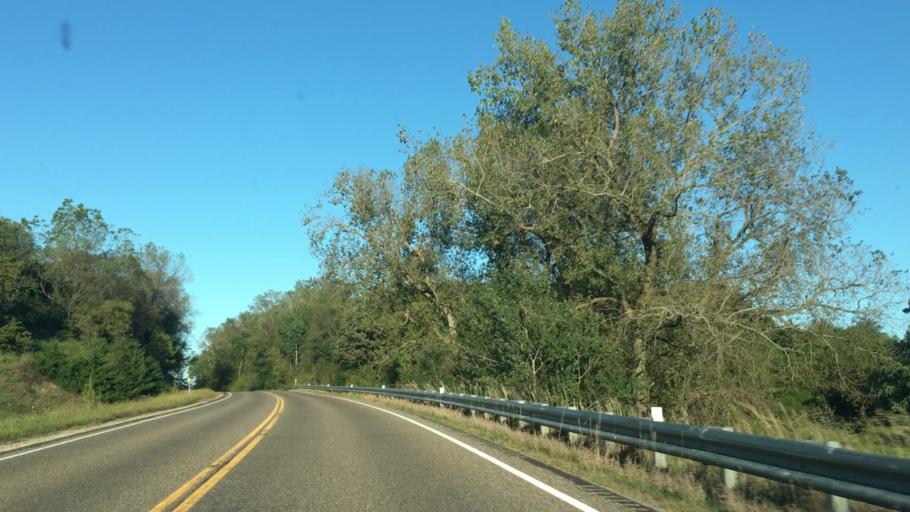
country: US
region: Minnesota
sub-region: Fillmore County
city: Chatfield
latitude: 43.8512
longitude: -92.1421
